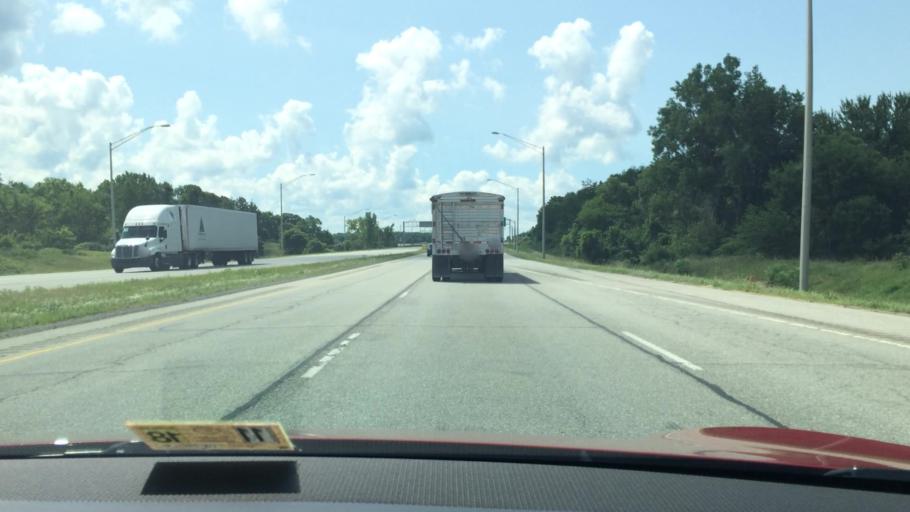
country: US
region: Indiana
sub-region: Saint Joseph County
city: South Bend
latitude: 41.7140
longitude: -86.3394
